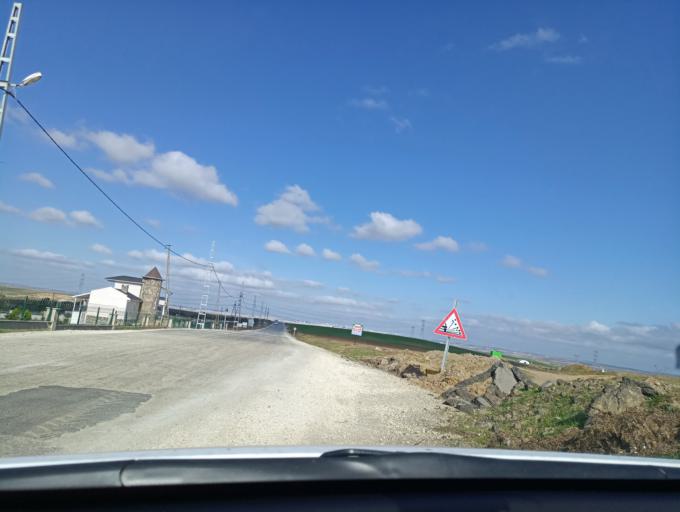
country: TR
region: Tekirdag
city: Corlu
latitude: 41.0511
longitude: 27.8355
